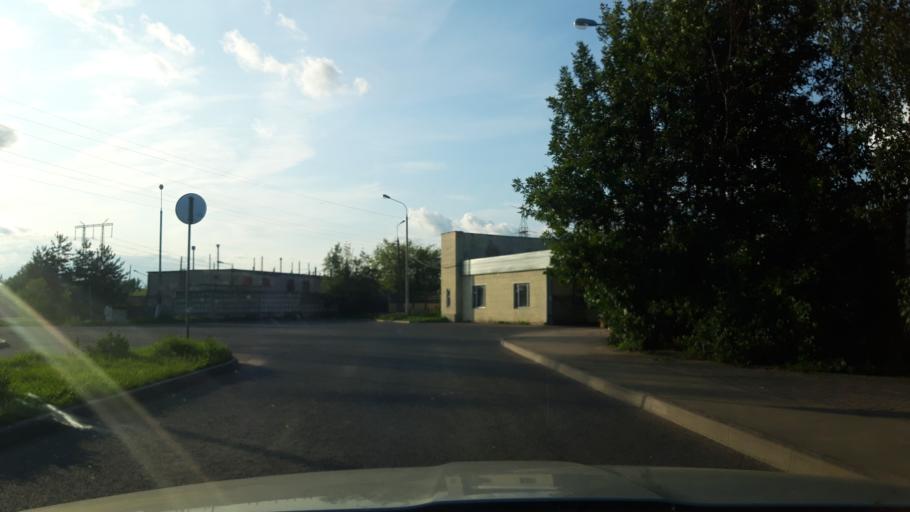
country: RU
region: Moskovskaya
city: Alabushevo
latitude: 56.0115
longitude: 37.1592
